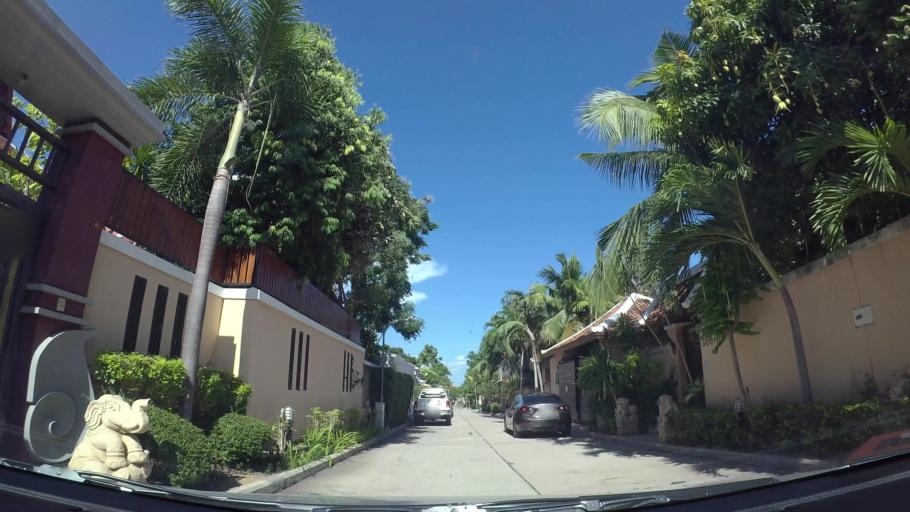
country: TH
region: Chon Buri
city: Phatthaya
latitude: 12.9079
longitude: 100.8716
